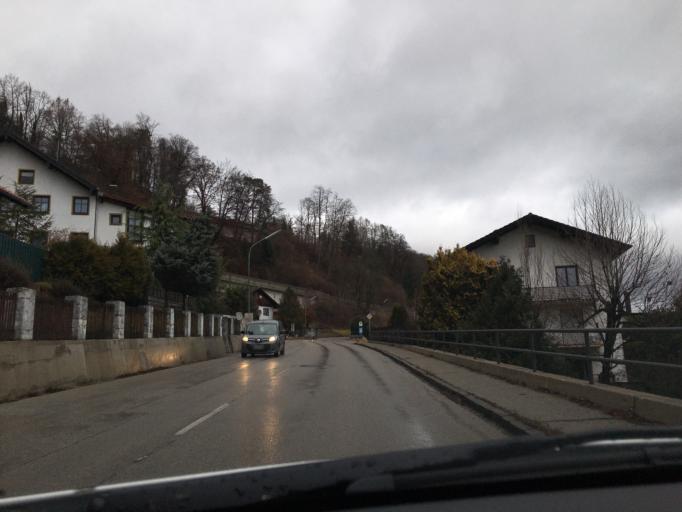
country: DE
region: Bavaria
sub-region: Upper Bavaria
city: Wolfratshausen
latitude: 47.9220
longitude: 11.4215
